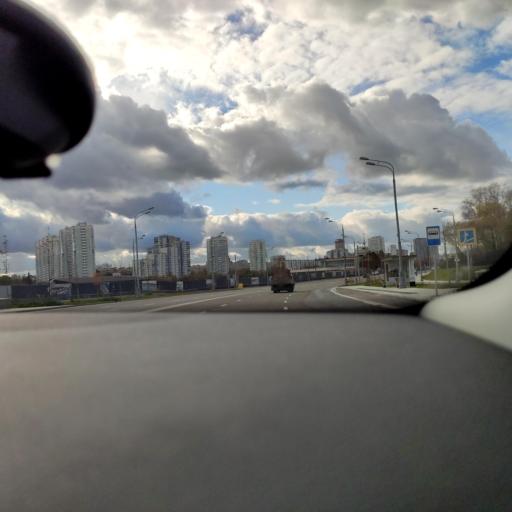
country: RU
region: Moskovskaya
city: Kozhukhovo
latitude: 55.6920
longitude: 37.6794
